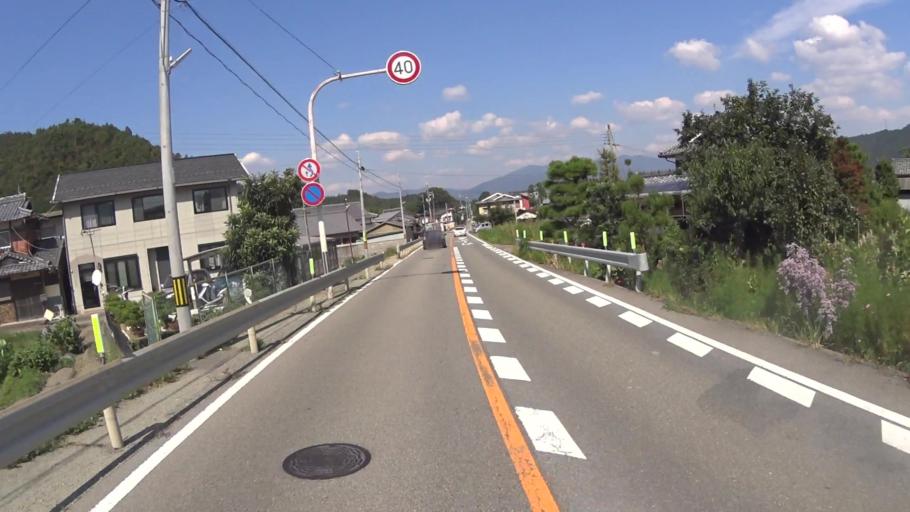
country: JP
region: Kyoto
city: Kameoka
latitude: 34.9940
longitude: 135.5363
